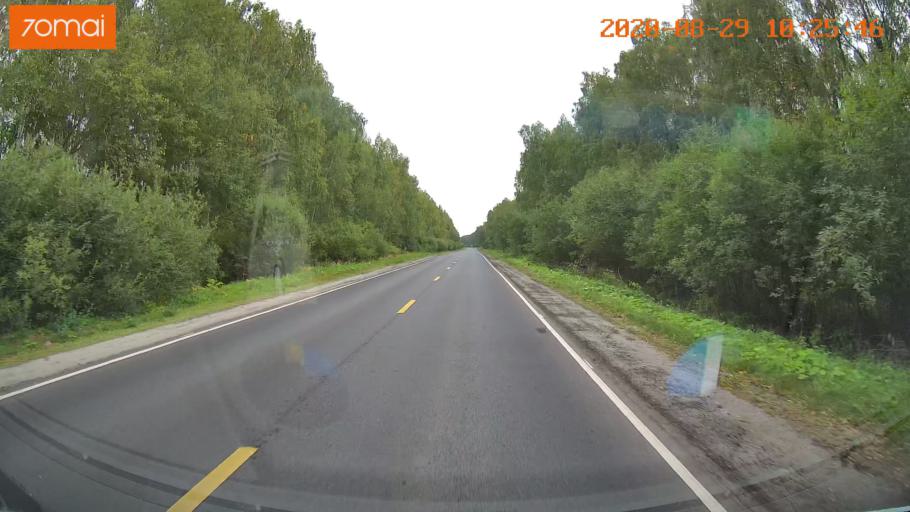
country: RU
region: Ivanovo
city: Yur'yevets
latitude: 57.3161
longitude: 43.0412
